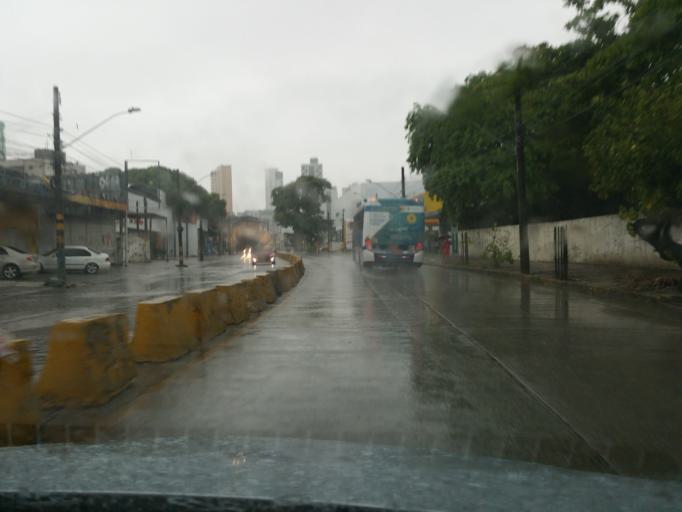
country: BR
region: Pernambuco
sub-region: Recife
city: Recife
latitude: -8.0394
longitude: -34.8885
